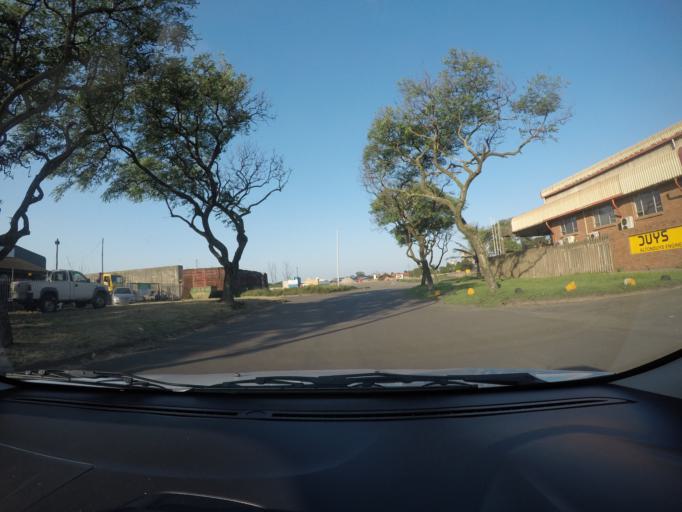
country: ZA
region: KwaZulu-Natal
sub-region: uThungulu District Municipality
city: Richards Bay
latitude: -28.7612
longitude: 32.0060
